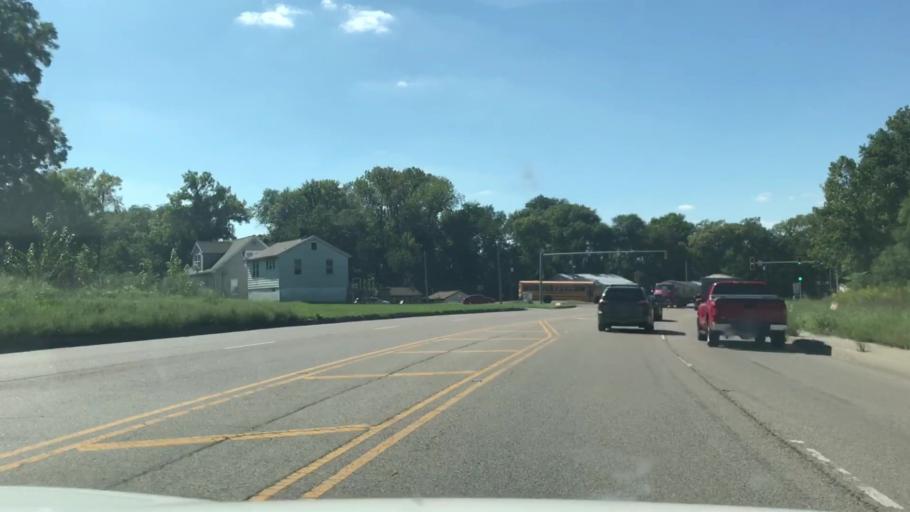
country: US
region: Illinois
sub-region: Saint Clair County
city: Swansea
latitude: 38.5420
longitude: -90.0465
